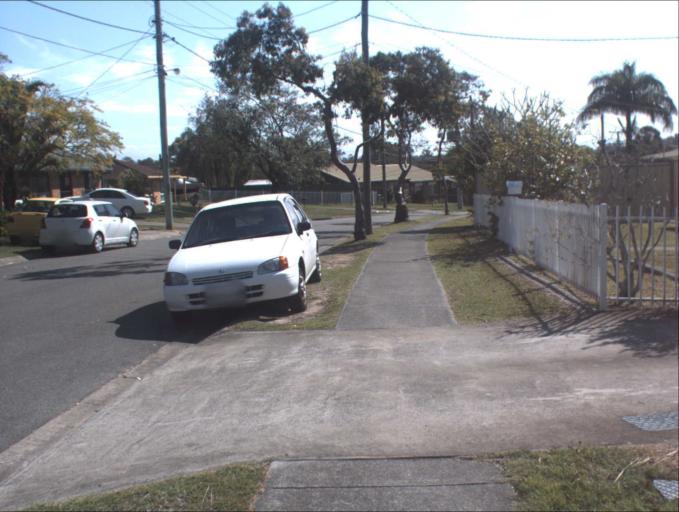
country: AU
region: Queensland
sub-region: Logan
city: Logan City
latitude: -27.6759
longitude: 153.0966
